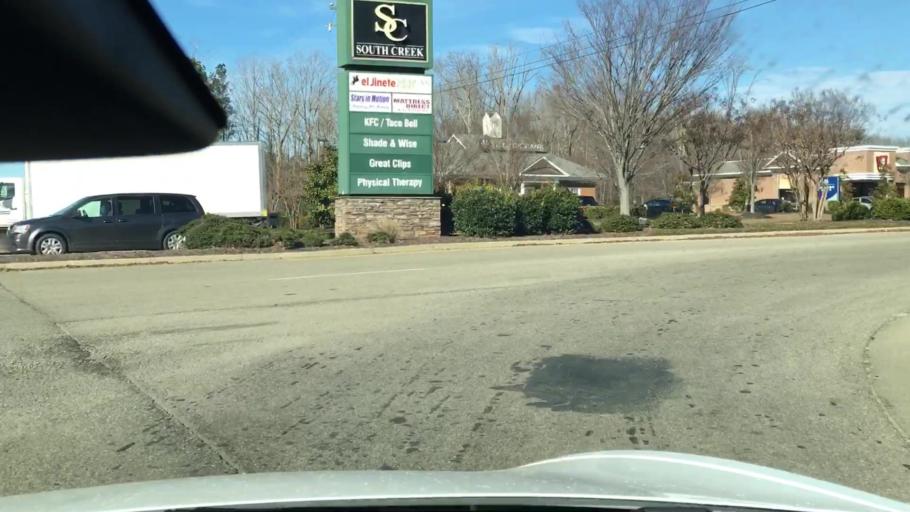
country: US
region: Virginia
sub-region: Powhatan County
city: Powhatan
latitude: 37.5147
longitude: -77.7917
